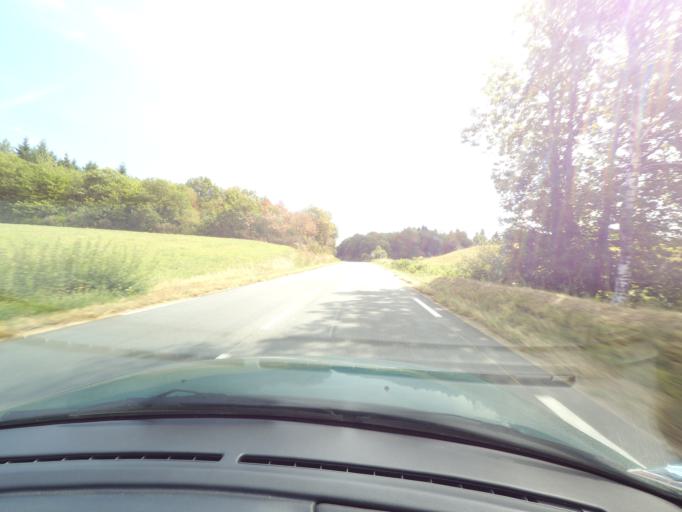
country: FR
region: Limousin
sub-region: Departement de la Haute-Vienne
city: Eymoutiers
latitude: 45.7354
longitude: 1.6866
